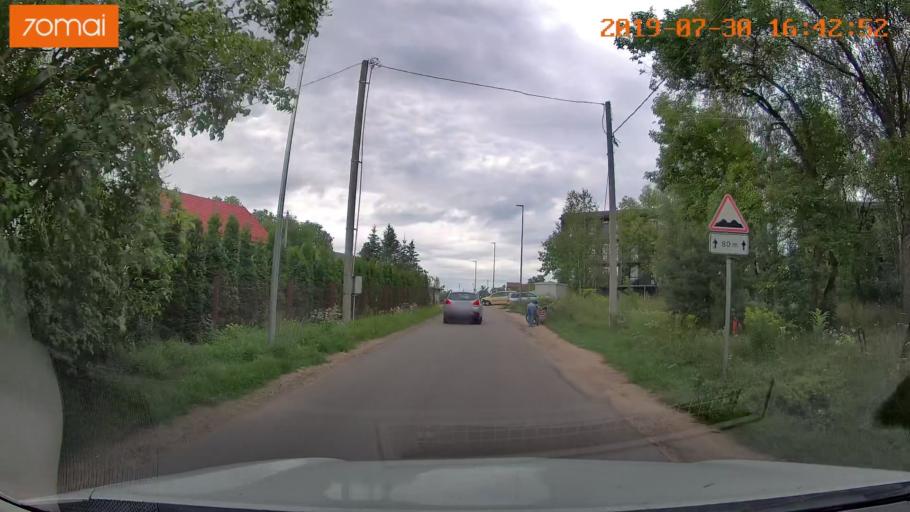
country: LT
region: Vilnius County
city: Rasos
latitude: 54.7178
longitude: 25.3514
